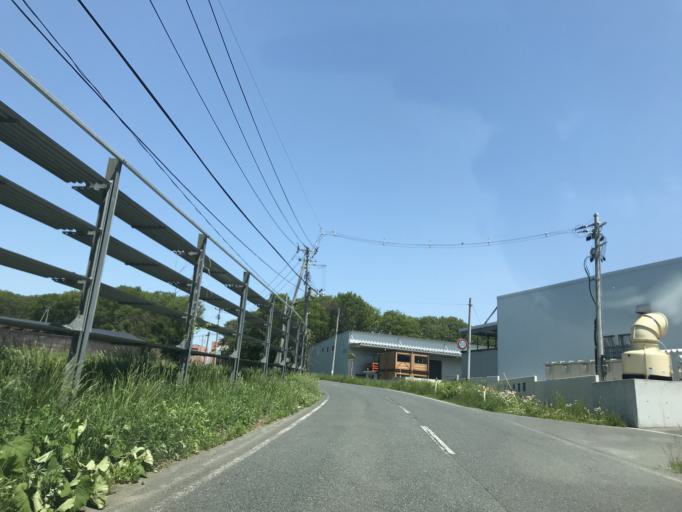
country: JP
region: Iwate
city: Kitakami
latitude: 39.2087
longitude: 141.0665
